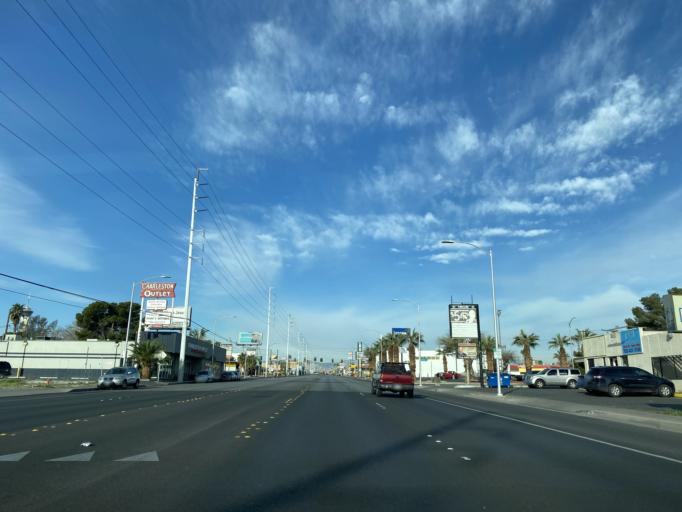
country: US
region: Nevada
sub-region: Clark County
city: Las Vegas
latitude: 36.1589
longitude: -115.1304
